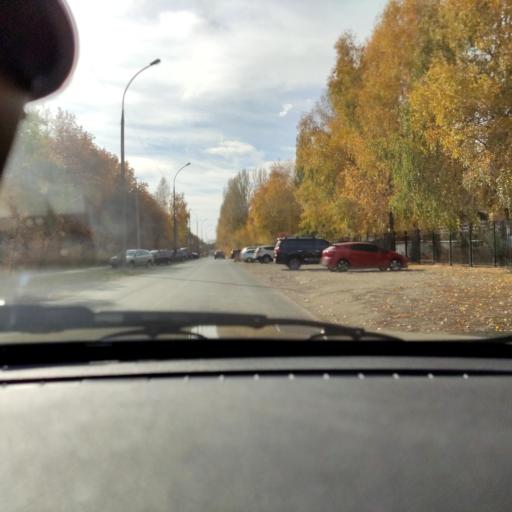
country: RU
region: Samara
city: Tol'yatti
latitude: 53.5059
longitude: 49.3057
